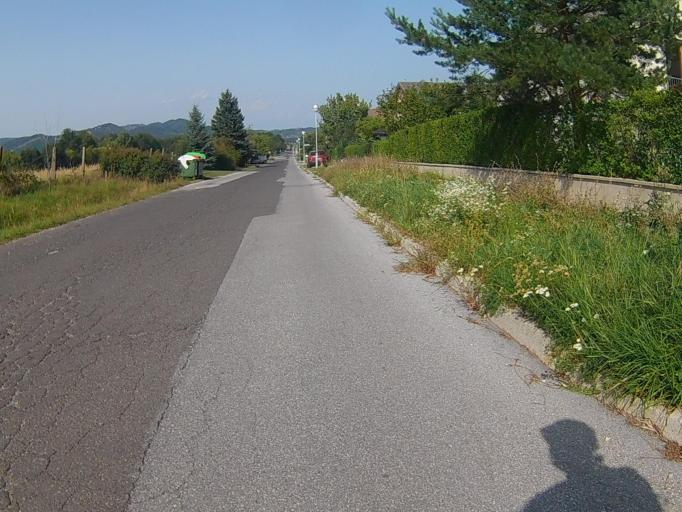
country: SI
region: Maribor
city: Pekre
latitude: 46.5402
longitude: 15.5893
